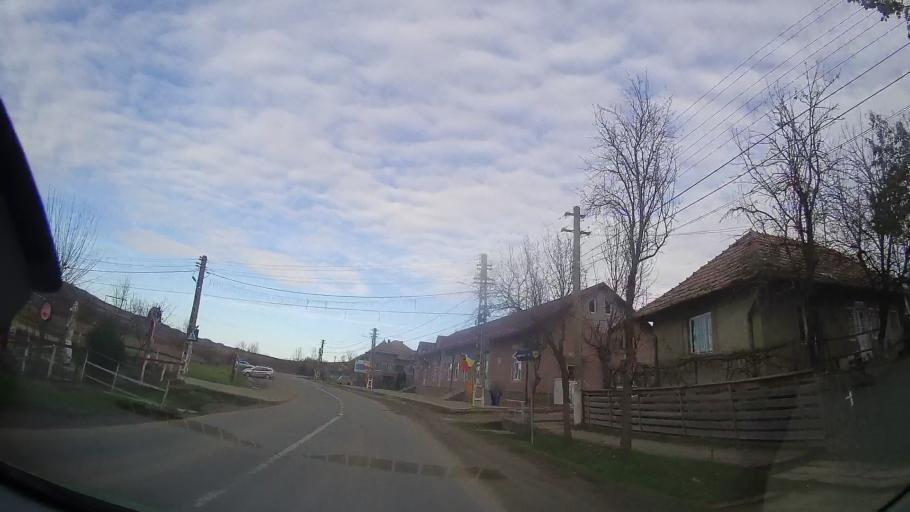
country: RO
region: Cluj
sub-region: Comuna Geaca
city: Geaca
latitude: 46.8566
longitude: 24.0889
